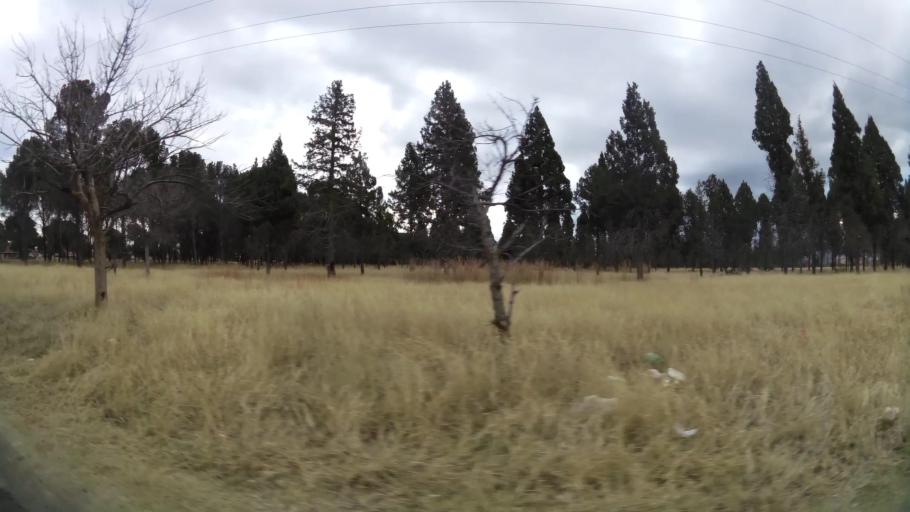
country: ZA
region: Orange Free State
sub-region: Lejweleputswa District Municipality
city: Welkom
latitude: -27.9729
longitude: 26.7005
